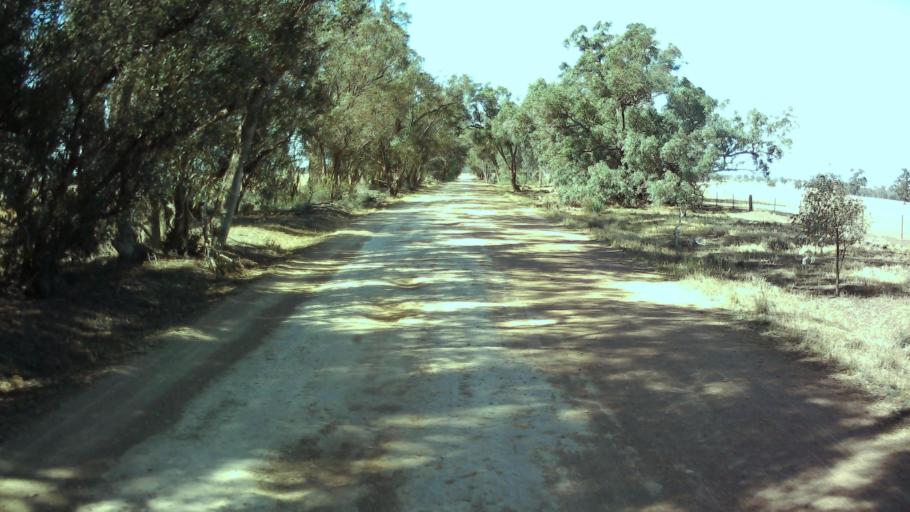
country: AU
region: New South Wales
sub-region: Weddin
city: Grenfell
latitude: -34.0501
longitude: 148.3140
